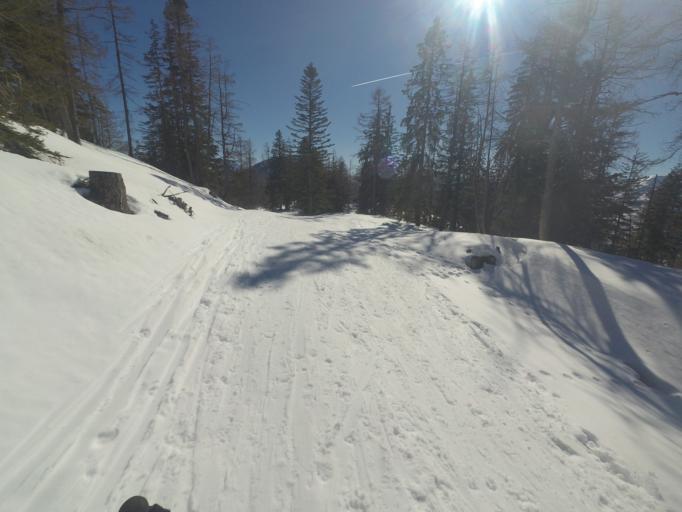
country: AT
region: Upper Austria
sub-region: Politischer Bezirk Gmunden
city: Sankt Wolfgang im Salzkammergut
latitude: 47.6621
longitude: 13.3865
